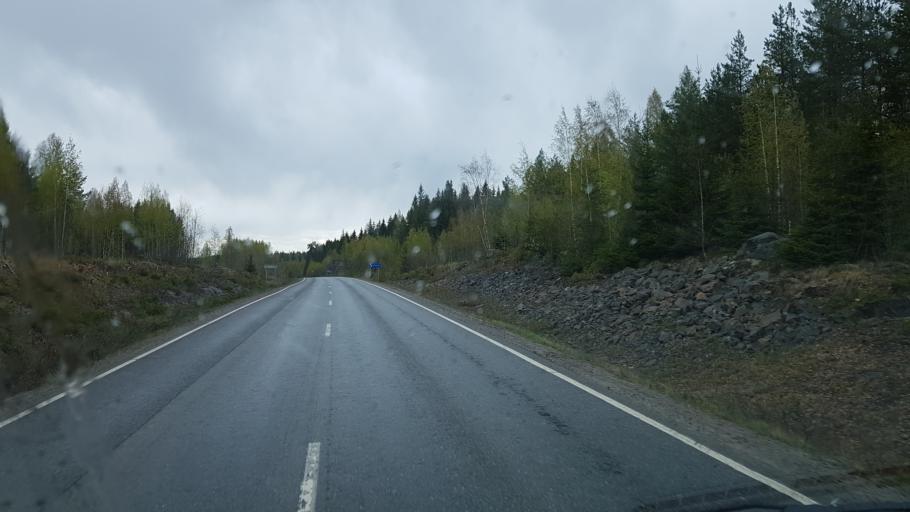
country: FI
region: Pirkanmaa
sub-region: Tampere
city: Pirkkala
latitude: 61.4045
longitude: 23.6322
